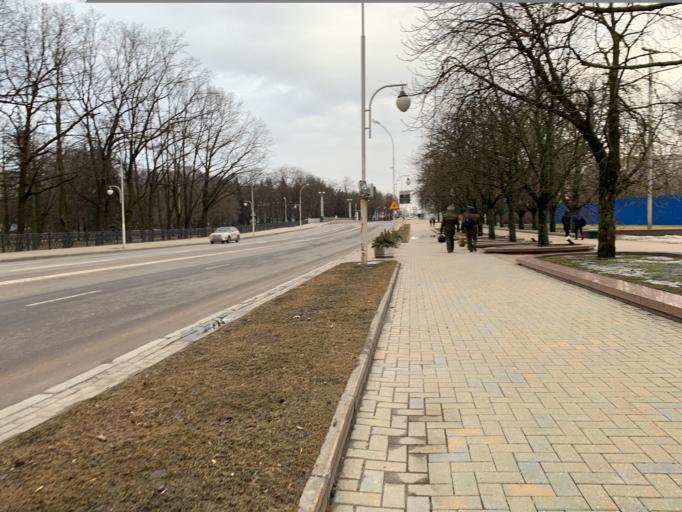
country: BY
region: Minsk
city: Minsk
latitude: 53.9076
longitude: 27.5618
